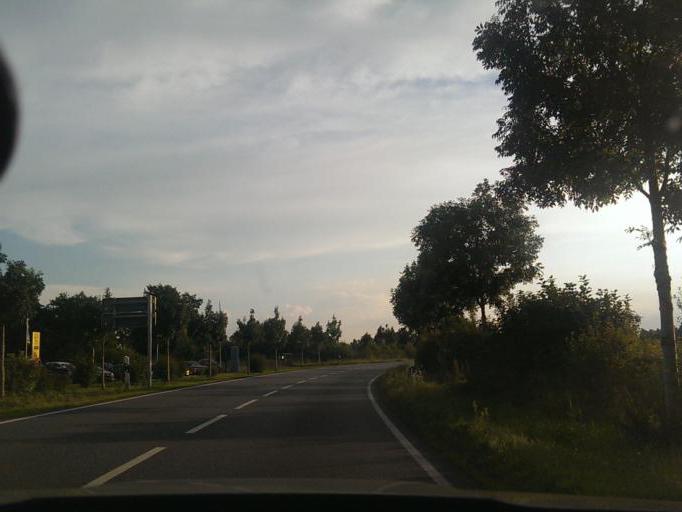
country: DE
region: Lower Saxony
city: Lilienthal
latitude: 53.1604
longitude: 8.9128
